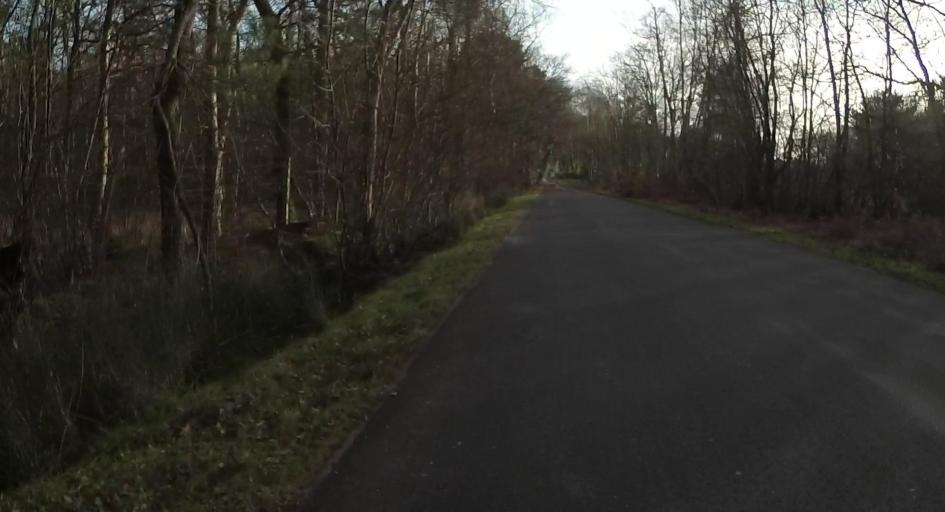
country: GB
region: England
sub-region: Bracknell Forest
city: Crowthorne
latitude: 51.3784
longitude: -0.8141
